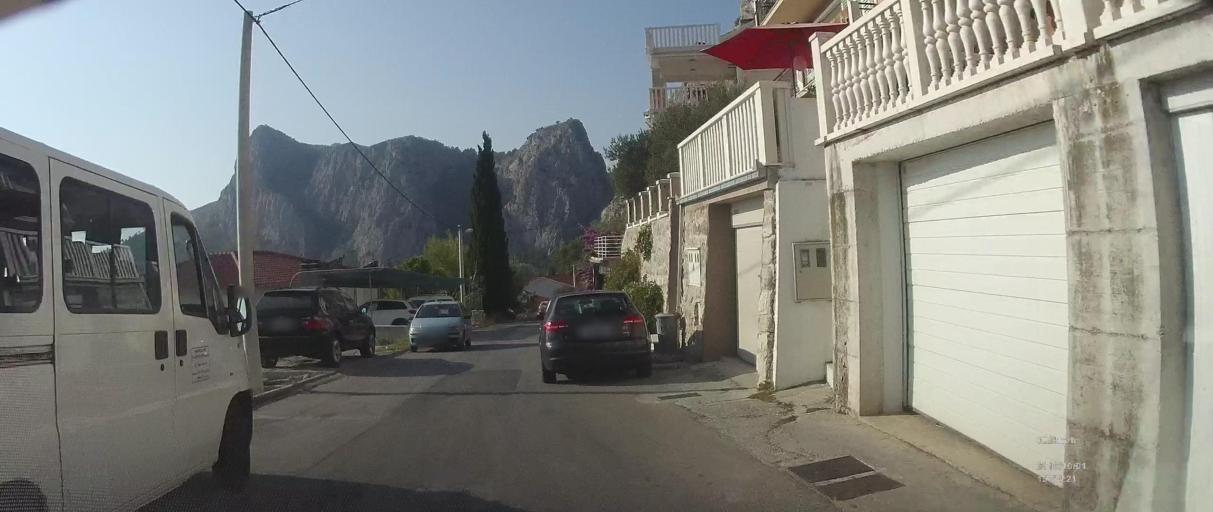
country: HR
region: Splitsko-Dalmatinska
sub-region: Grad Omis
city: Omis
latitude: 43.4422
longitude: 16.6971
